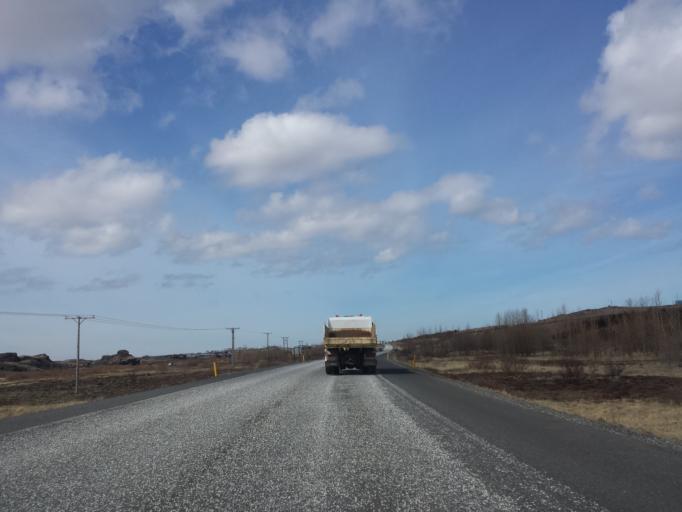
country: IS
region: Capital Region
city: Mosfellsbaer
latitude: 64.0946
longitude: -21.7345
